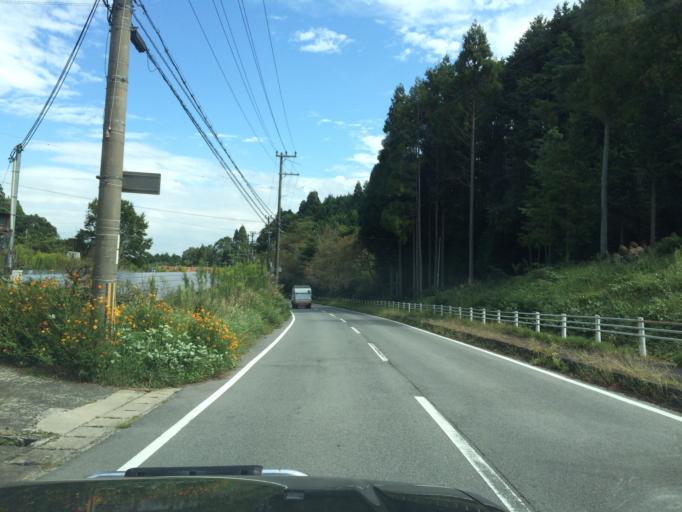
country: JP
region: Mie
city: Nabari
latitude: 34.6797
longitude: 135.9926
